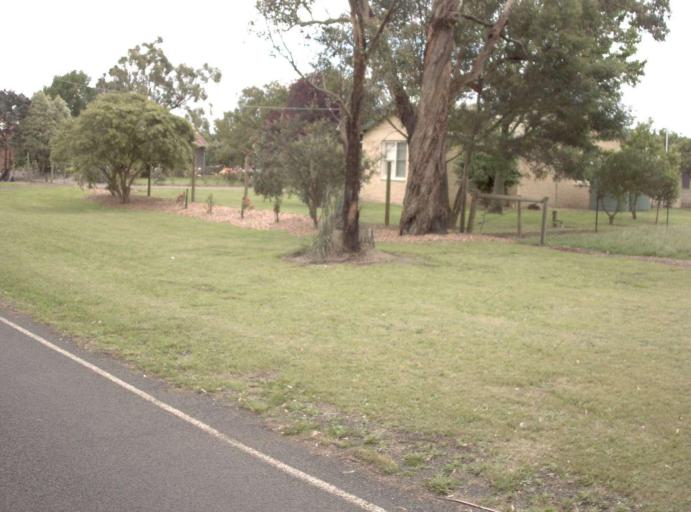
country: AU
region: Victoria
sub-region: Latrobe
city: Moe
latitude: -38.0138
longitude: 146.1498
